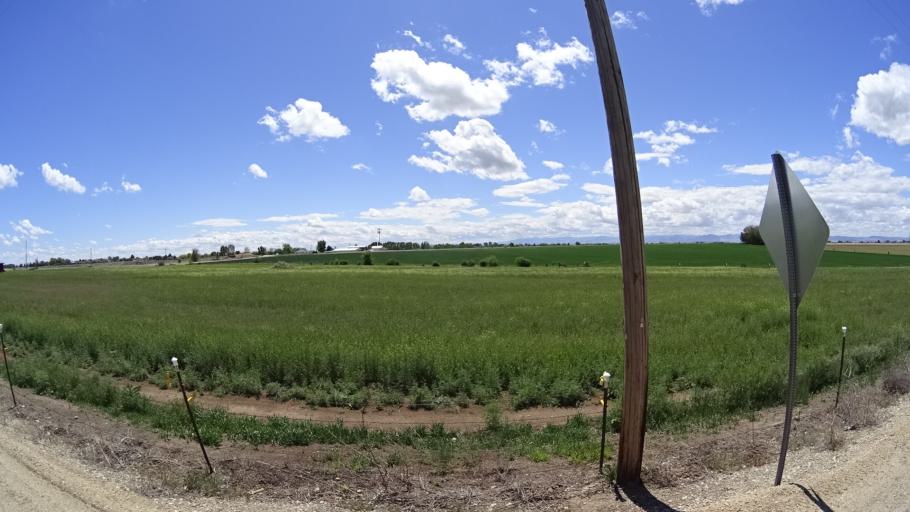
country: US
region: Idaho
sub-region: Ada County
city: Meridian
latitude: 43.5903
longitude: -116.4557
